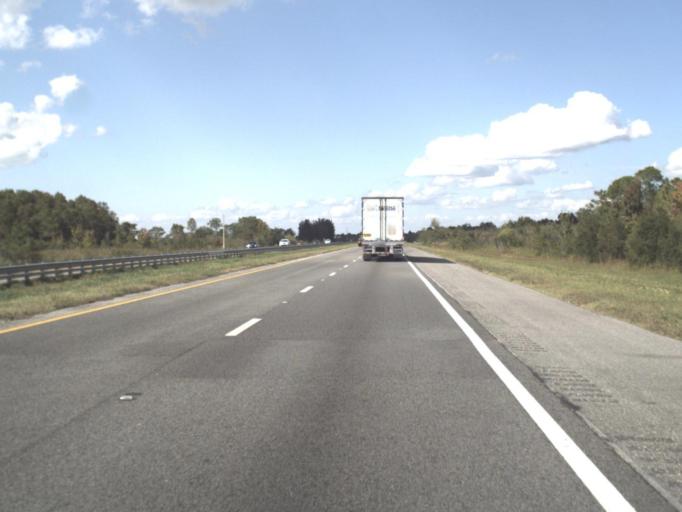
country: US
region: Florida
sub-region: Indian River County
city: Fellsmere
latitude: 27.7741
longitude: -80.9640
